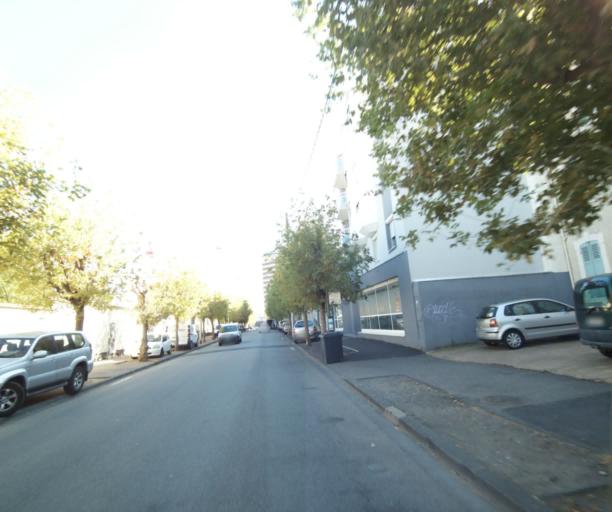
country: FR
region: Auvergne
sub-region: Departement du Puy-de-Dome
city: Clermont-Ferrand
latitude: 45.7827
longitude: 3.1029
